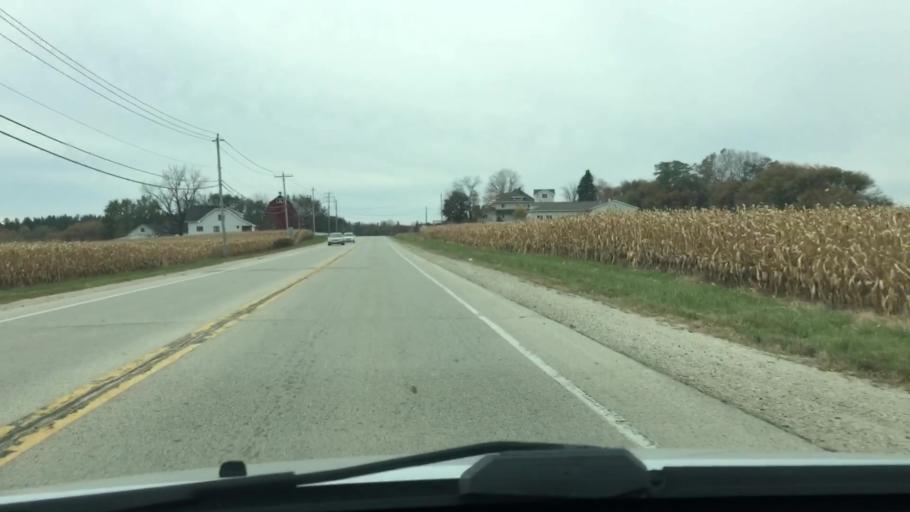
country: US
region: Wisconsin
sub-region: Waukesha County
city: New Berlin
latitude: 42.9628
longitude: -88.1312
